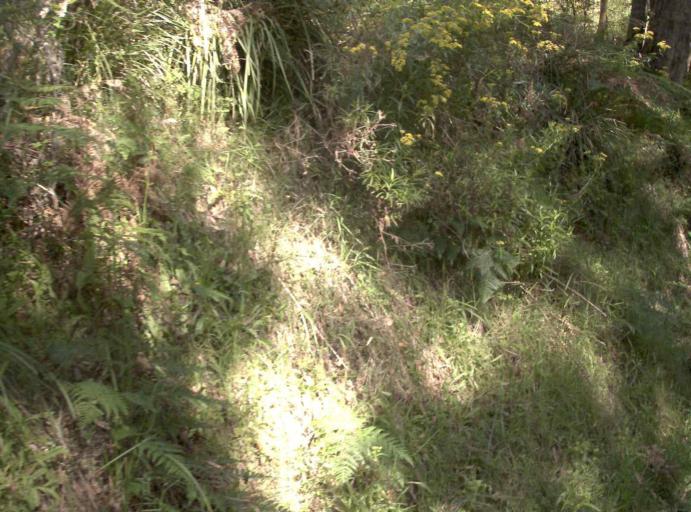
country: AU
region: New South Wales
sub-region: Bombala
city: Bombala
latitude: -37.3494
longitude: 148.6929
